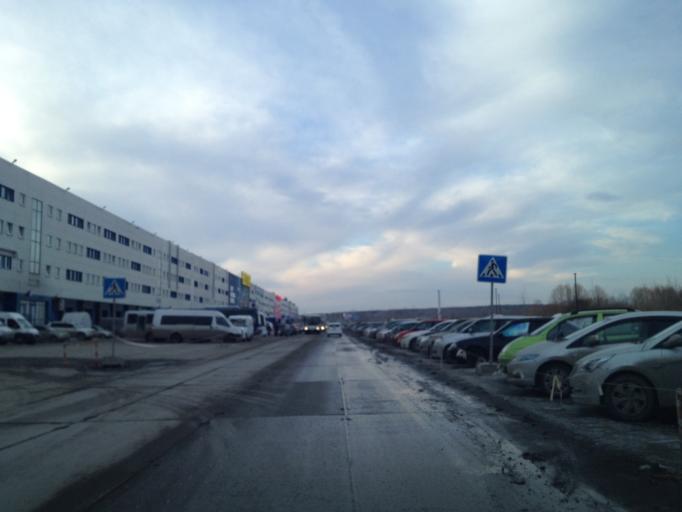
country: RU
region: Sverdlovsk
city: Istok
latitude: 56.7591
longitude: 60.7563
